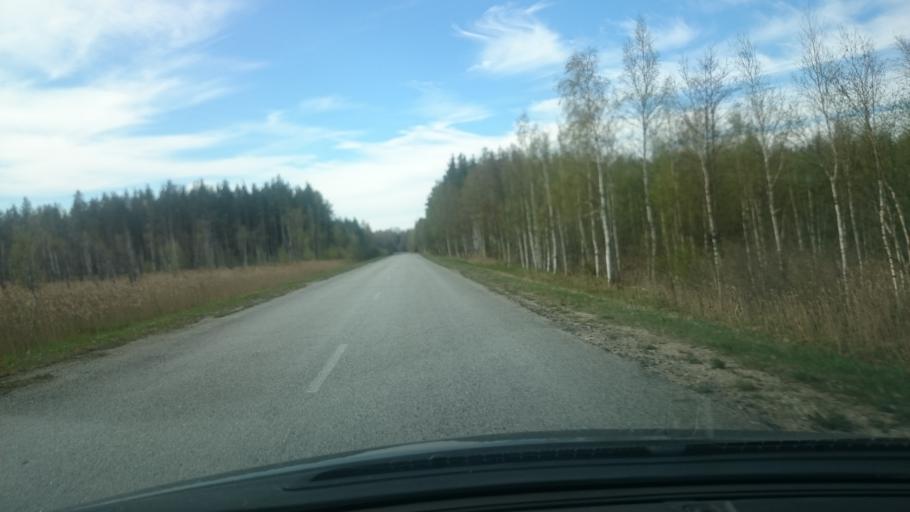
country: EE
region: Ida-Virumaa
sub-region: Toila vald
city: Voka
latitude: 59.1181
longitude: 27.6319
